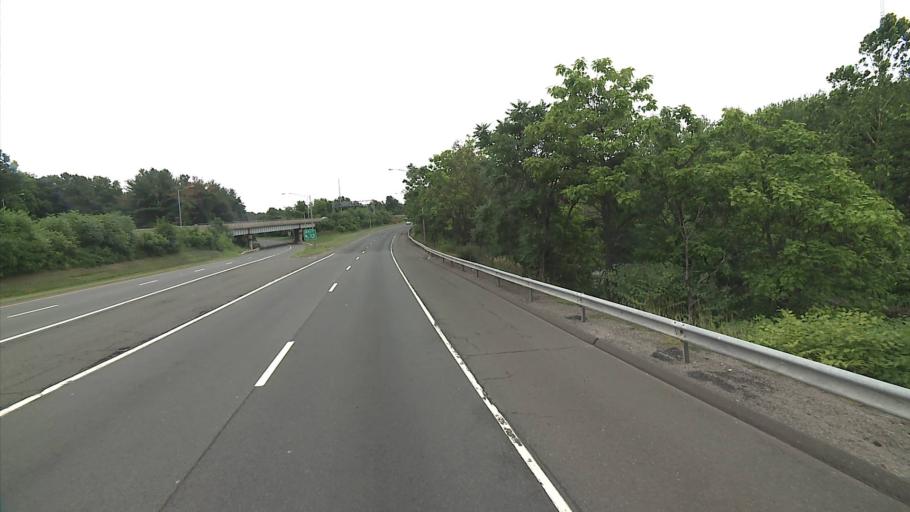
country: US
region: Connecticut
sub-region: New Haven County
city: Waterbury
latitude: 41.5659
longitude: -73.0578
